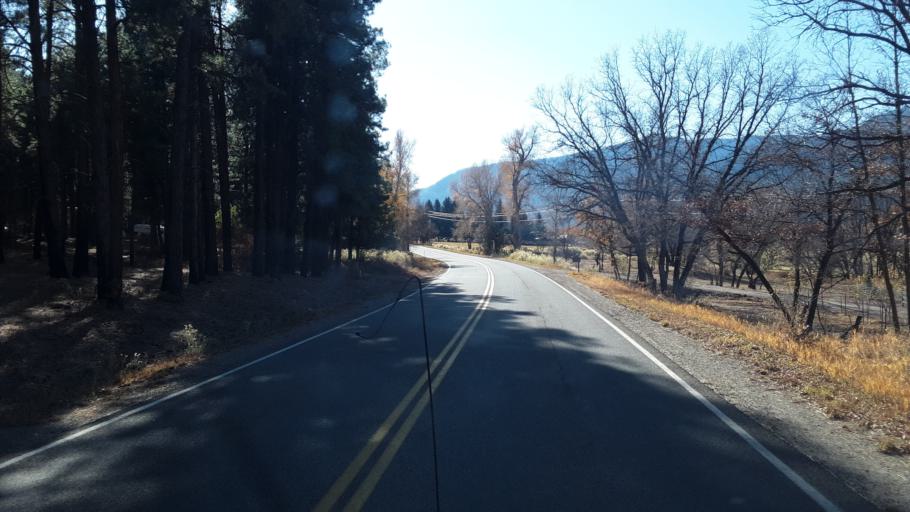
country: US
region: Colorado
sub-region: La Plata County
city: Durango
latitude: 37.4003
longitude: -107.8187
